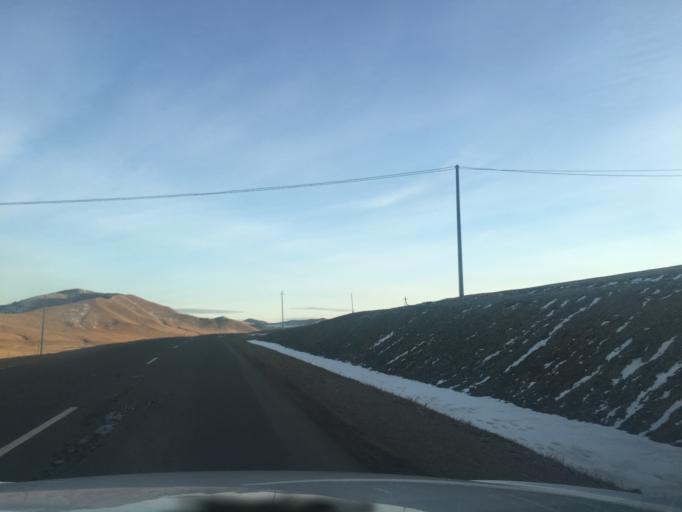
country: MN
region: Central Aimak
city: Mandal
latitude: 48.1960
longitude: 106.7079
